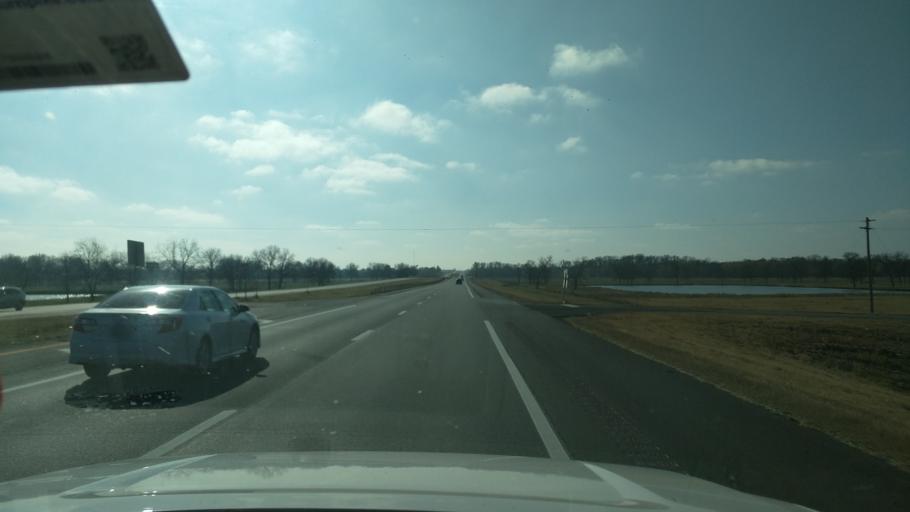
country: US
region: Oklahoma
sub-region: Washington County
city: Bartlesville
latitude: 36.6544
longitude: -95.9356
